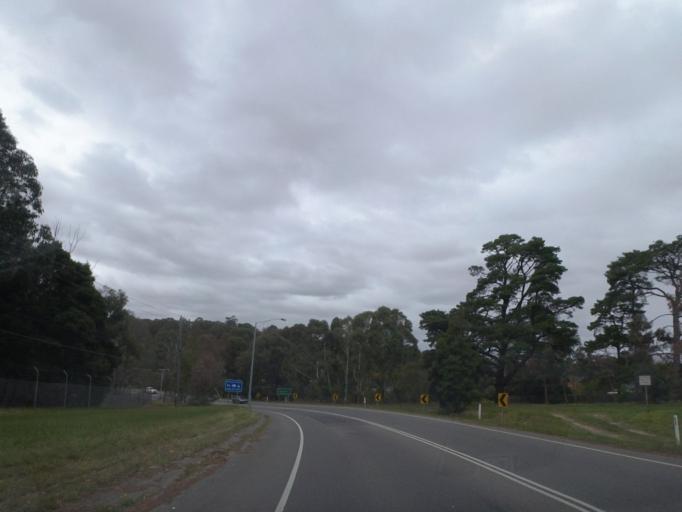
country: AU
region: Victoria
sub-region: Nillumbik
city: Eltham
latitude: -37.7522
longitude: 145.1711
